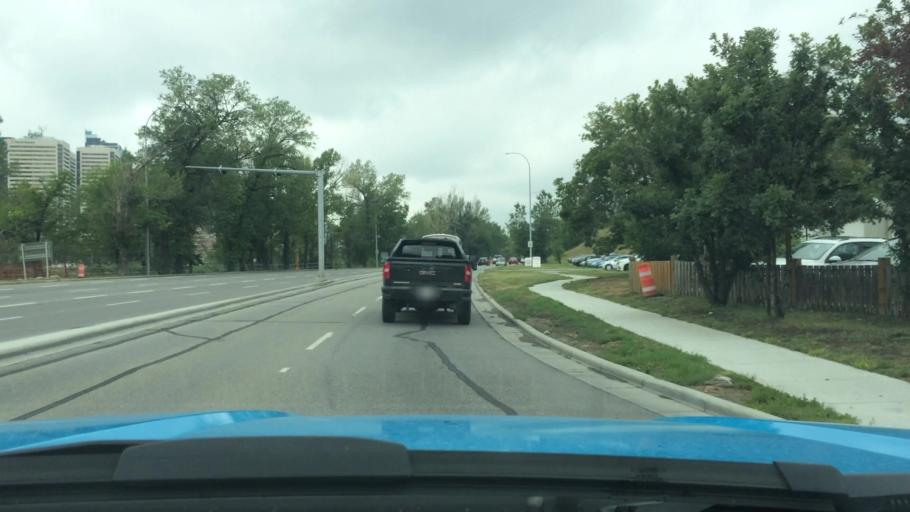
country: CA
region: Alberta
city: Calgary
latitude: 51.0511
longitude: -114.0521
